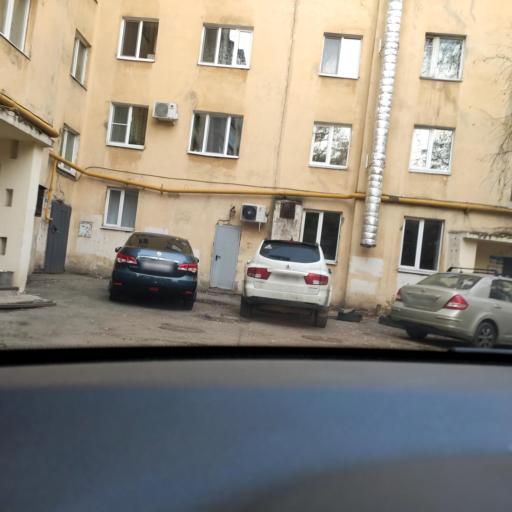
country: RU
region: Samara
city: Samara
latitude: 53.1919
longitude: 50.1800
